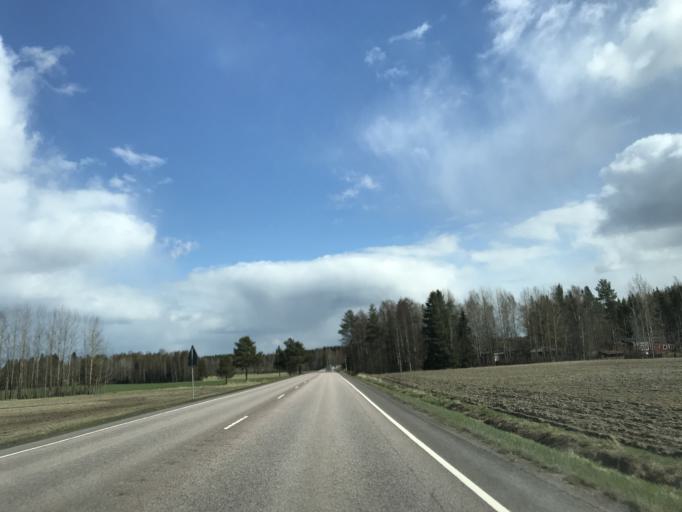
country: FI
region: Uusimaa
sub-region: Helsinki
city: Hyvinge
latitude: 60.5381
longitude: 24.9024
